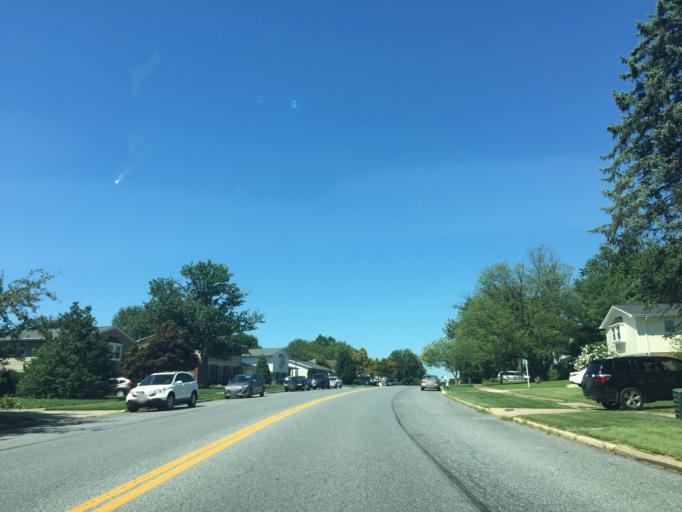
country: US
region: Maryland
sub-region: Baltimore County
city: Timonium
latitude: 39.4553
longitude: -76.6176
